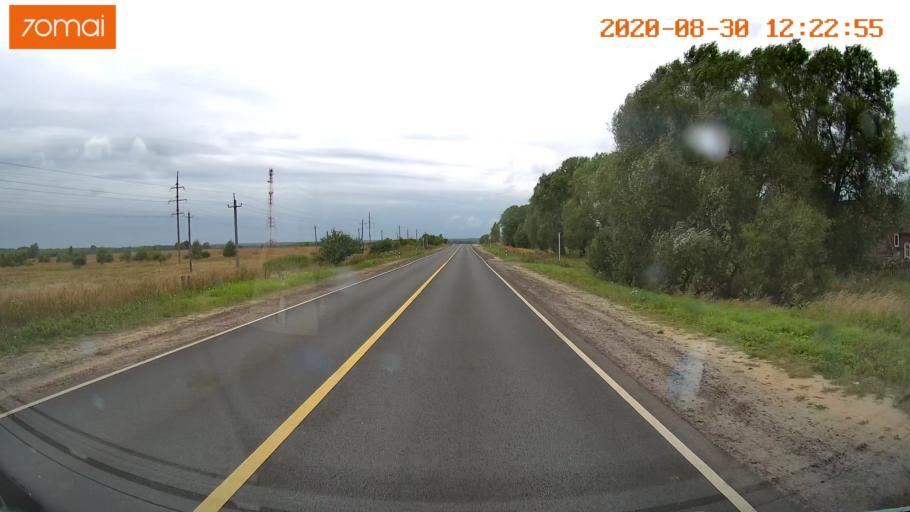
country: RU
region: Ivanovo
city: Yur'yevets
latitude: 57.3313
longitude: 42.8379
